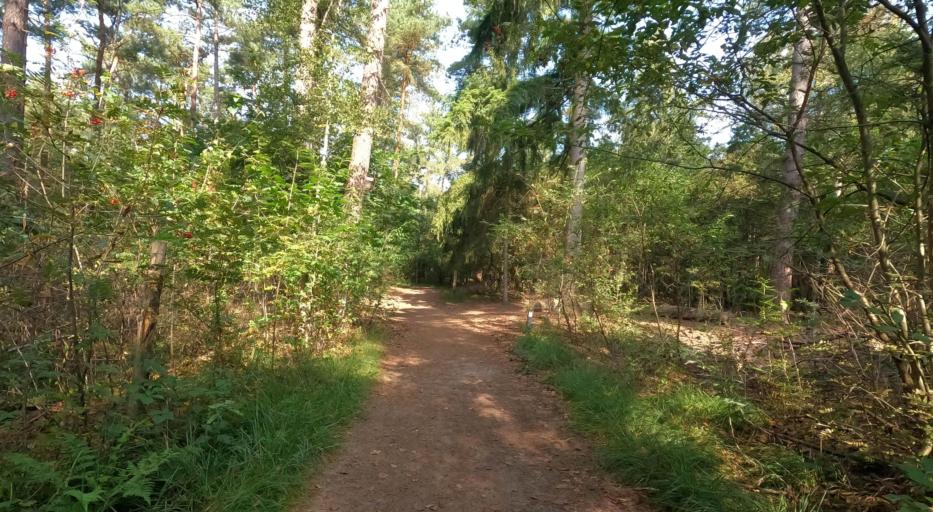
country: BE
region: Flanders
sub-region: Provincie Antwerpen
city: Essen
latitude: 51.4337
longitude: 4.4590
